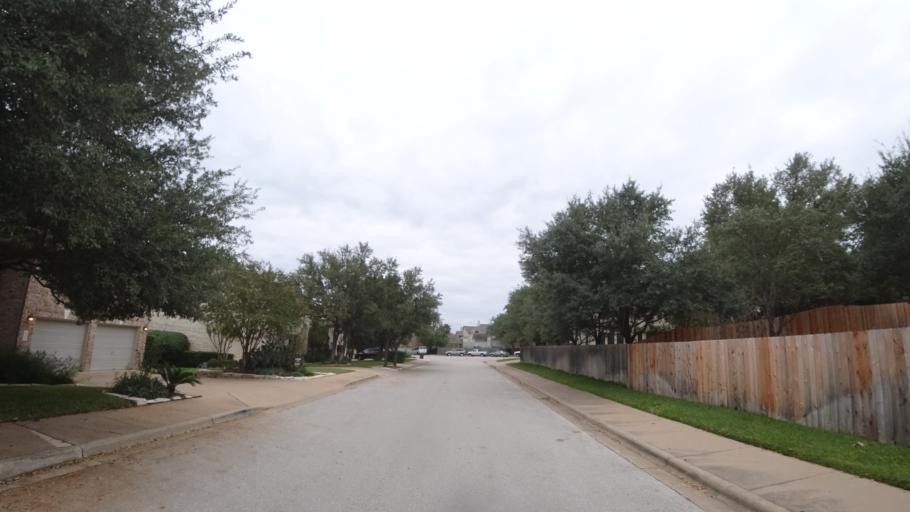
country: US
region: Texas
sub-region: Travis County
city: Bee Cave
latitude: 30.3126
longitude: -97.9216
